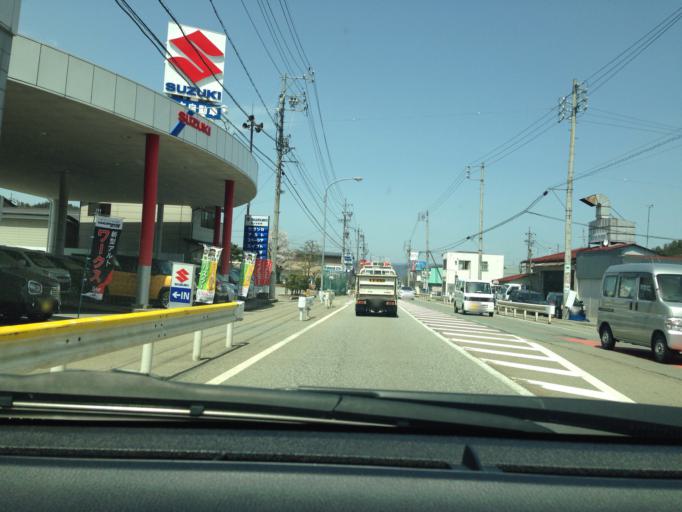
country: JP
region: Gifu
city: Takayama
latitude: 36.1156
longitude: 137.2640
